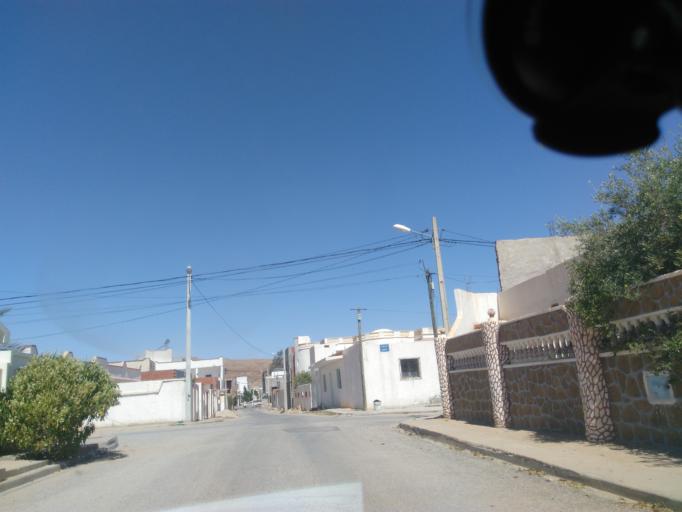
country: TN
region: Tataouine
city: Tataouine
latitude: 32.9479
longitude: 10.4665
